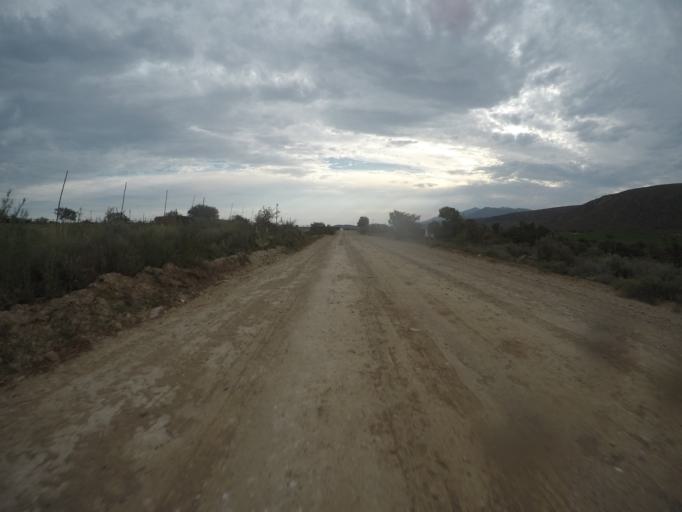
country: ZA
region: Eastern Cape
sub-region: Cacadu District Municipality
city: Willowmore
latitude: -33.4915
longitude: 23.5948
